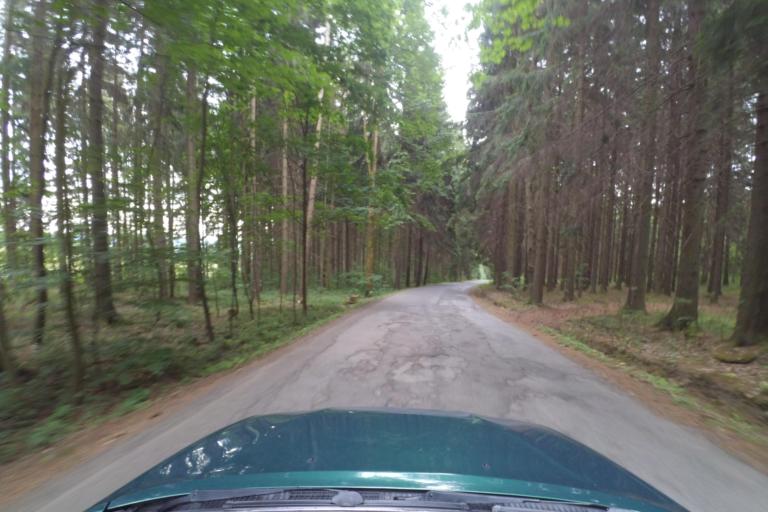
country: CZ
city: Plavy
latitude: 50.6808
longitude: 15.2968
